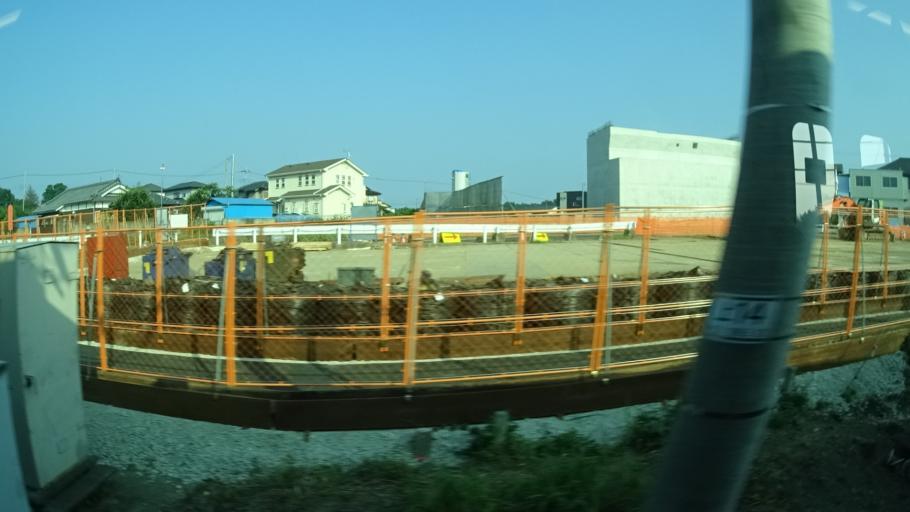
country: JP
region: Ibaraki
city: Takahagi
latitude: 36.6798
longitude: 140.6925
